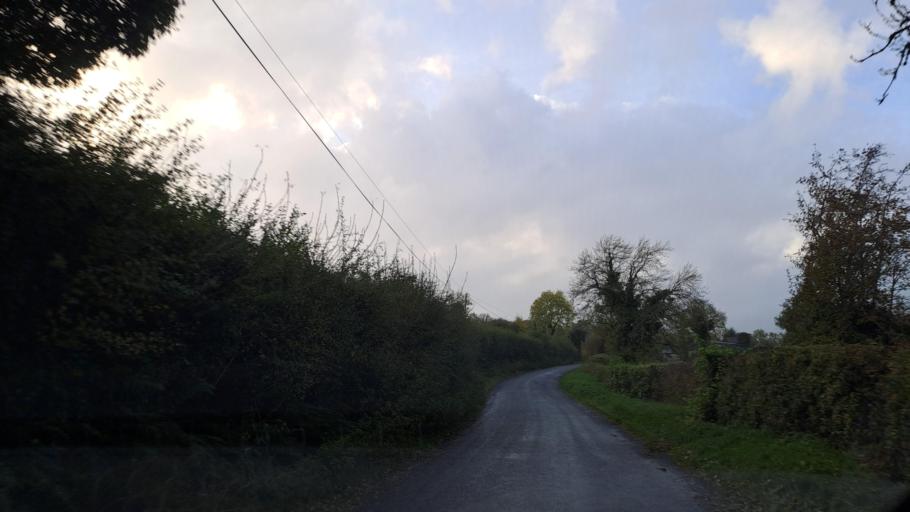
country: IE
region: Ulster
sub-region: County Monaghan
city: Carrickmacross
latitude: 53.9717
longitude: -6.7694
